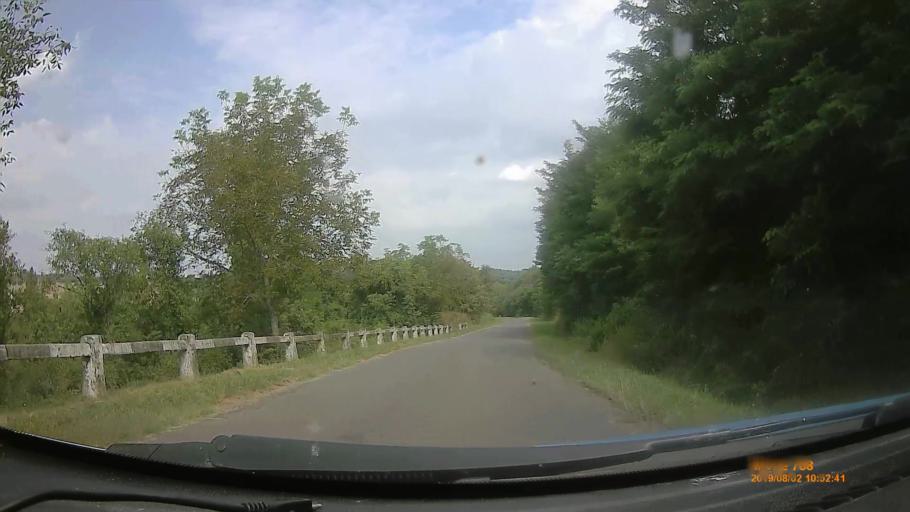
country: HU
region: Baranya
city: Buekkoesd
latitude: 46.0907
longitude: 17.9590
